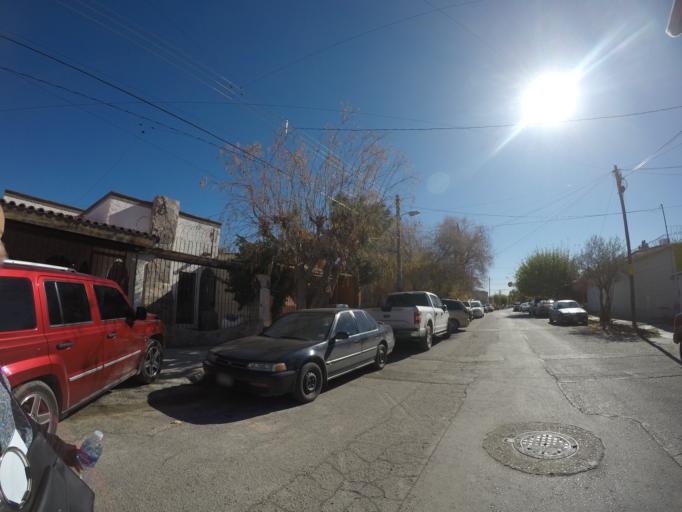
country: MX
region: Chihuahua
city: Ciudad Juarez
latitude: 31.7429
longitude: -106.4608
